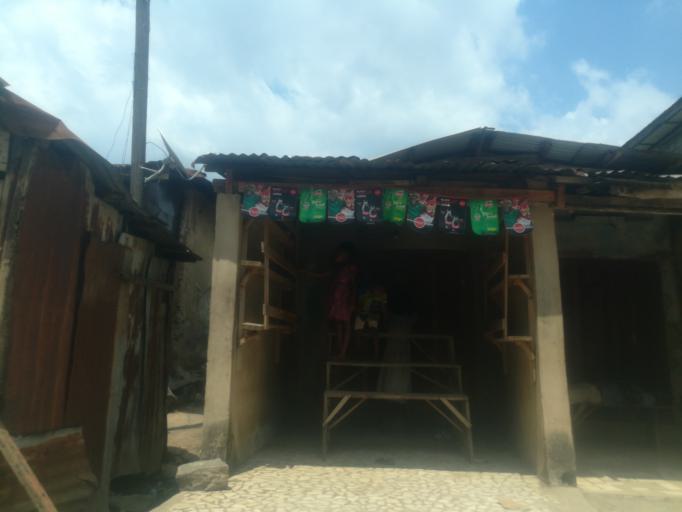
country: NG
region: Oyo
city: Ibadan
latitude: 7.3899
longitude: 3.8855
